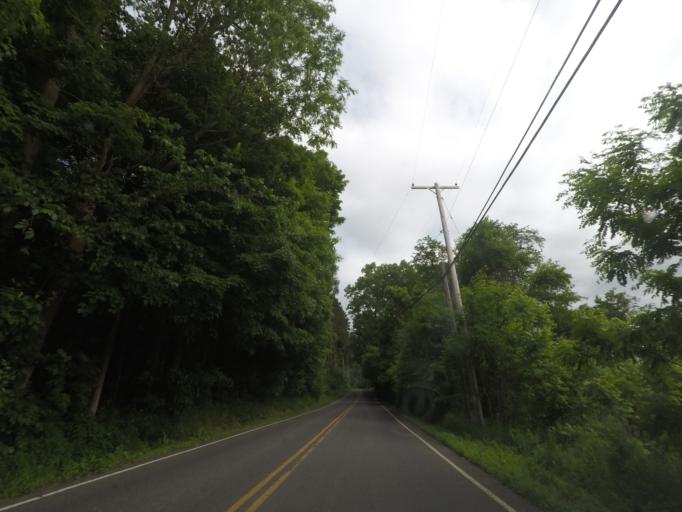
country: US
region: New York
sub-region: Dutchess County
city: Pine Plains
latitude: 42.0028
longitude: -73.5084
